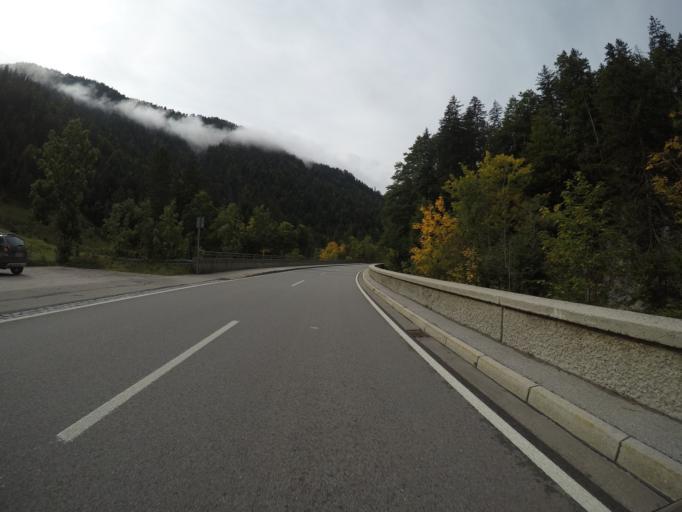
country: AT
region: Tyrol
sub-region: Politischer Bezirk Schwaz
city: Achenkirch
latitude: 47.5825
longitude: 11.6173
